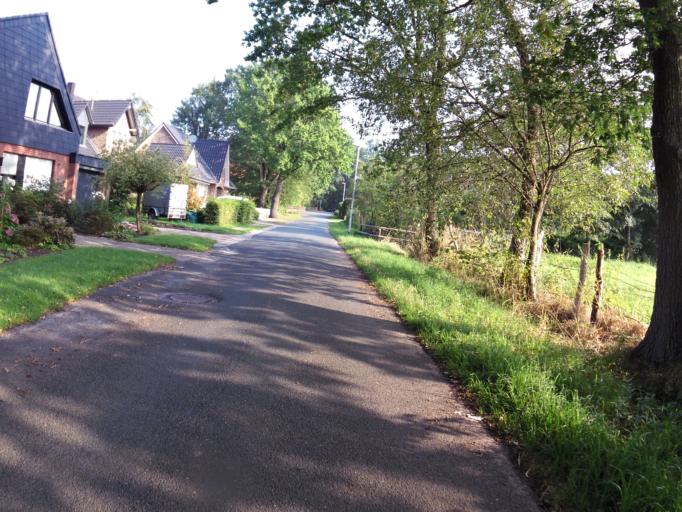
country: DE
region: Lower Saxony
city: Verden
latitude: 52.9412
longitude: 9.2273
